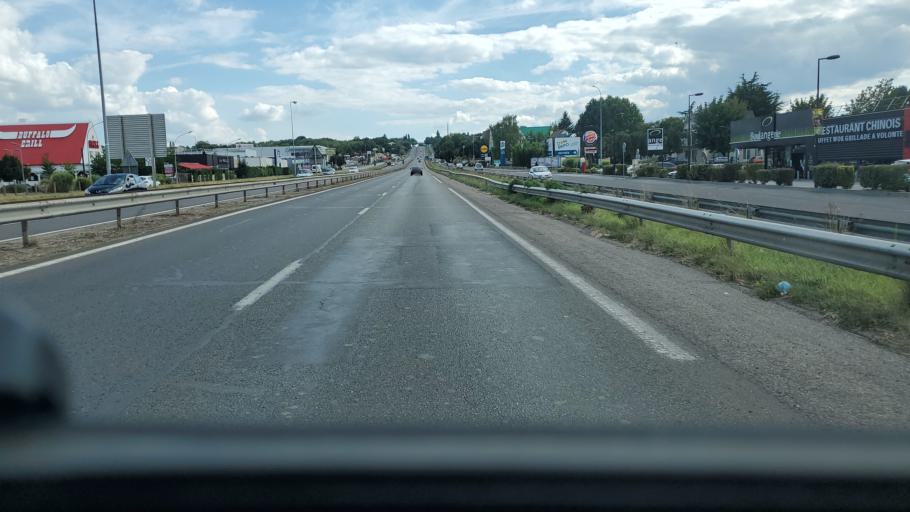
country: FR
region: Ile-de-France
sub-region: Departement de Seine-et-Marne
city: Meaux
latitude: 48.9411
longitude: 2.8794
